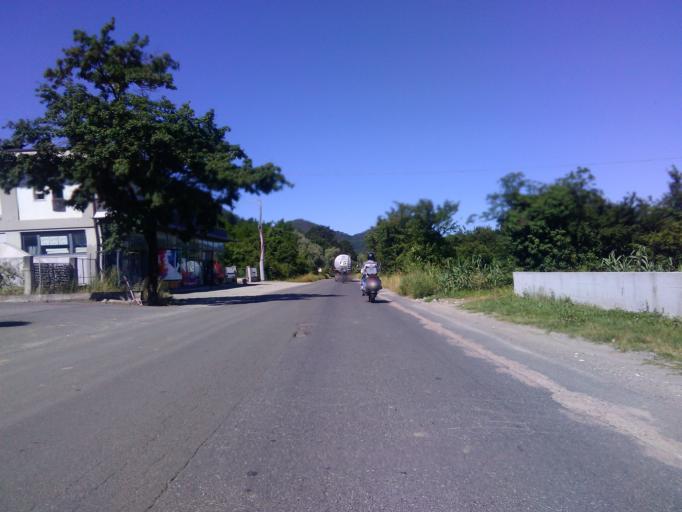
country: IT
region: Tuscany
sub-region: Provincia di Massa-Carrara
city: Pallerone
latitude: 44.2032
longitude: 10.0054
